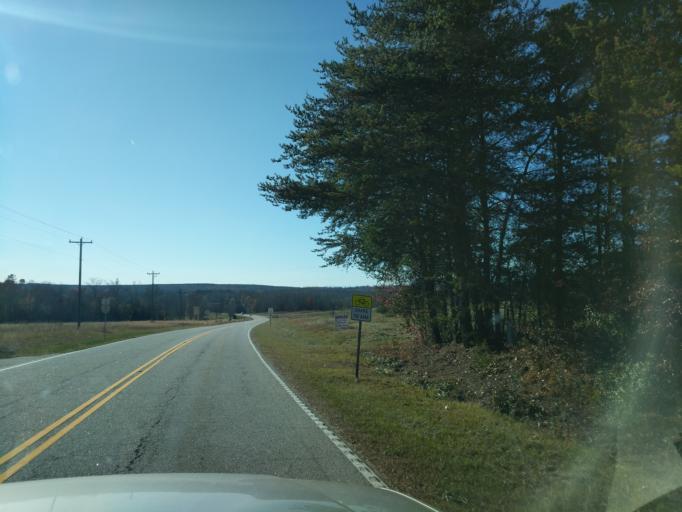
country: US
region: South Carolina
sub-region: Spartanburg County
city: Landrum
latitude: 35.1367
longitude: -82.1069
